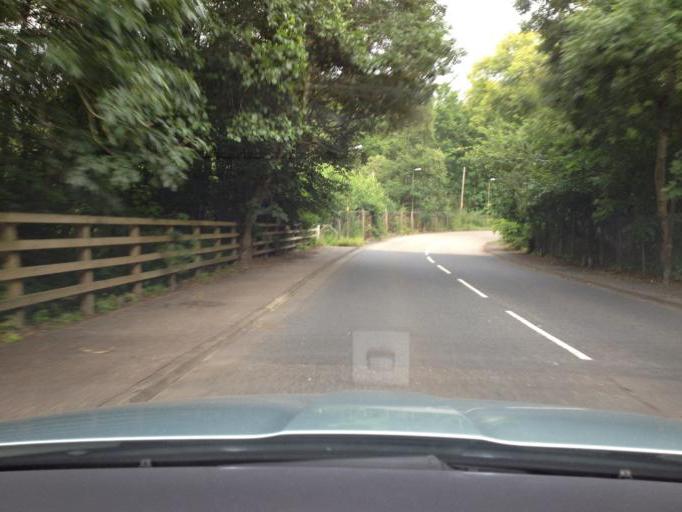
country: GB
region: Scotland
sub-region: West Lothian
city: Armadale
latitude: 55.9326
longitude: -3.6974
